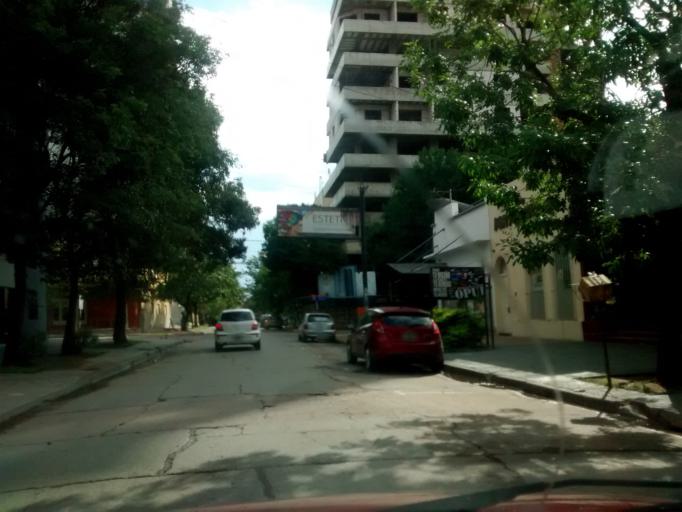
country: AR
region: Chaco
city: Resistencia
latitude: -27.4485
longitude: -58.9853
